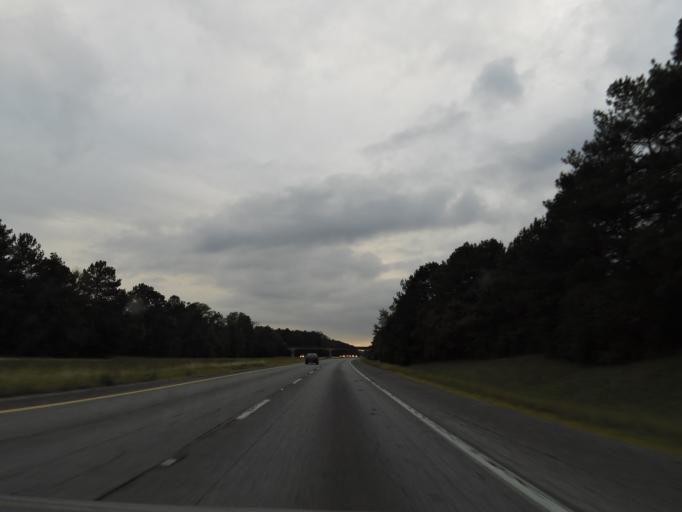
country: US
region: Alabama
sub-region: Saint Clair County
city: Ashville
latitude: 33.8114
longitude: -86.3567
